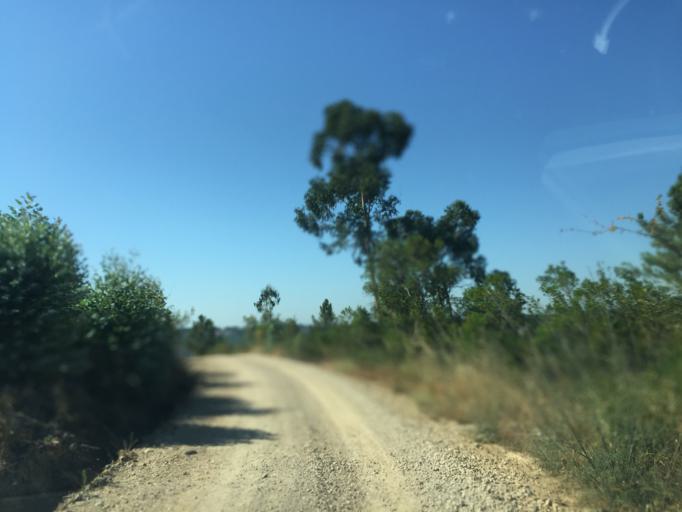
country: PT
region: Santarem
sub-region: Constancia
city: Constancia
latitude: 39.5514
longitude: -8.3251
